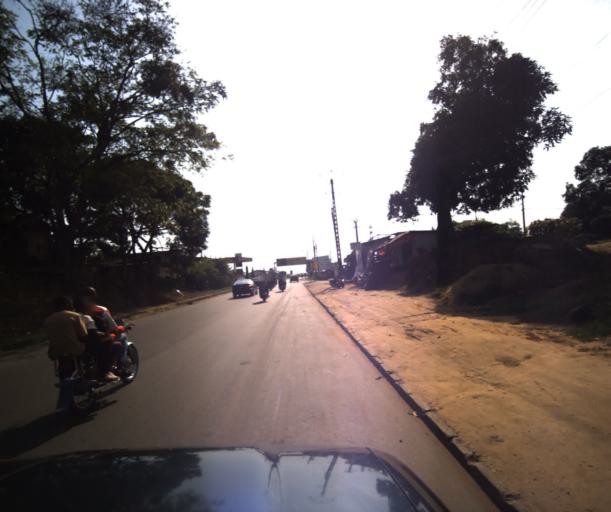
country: CM
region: Littoral
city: Bonaberi
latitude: 4.0705
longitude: 9.6880
